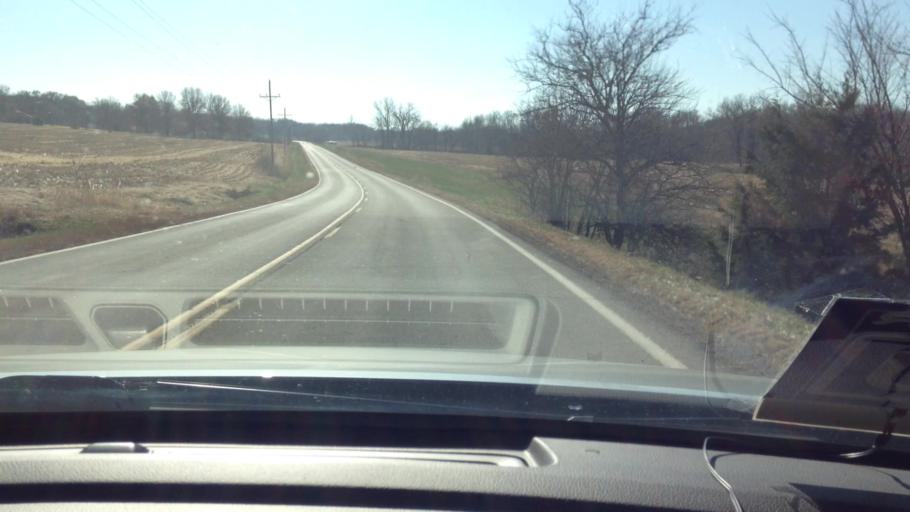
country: US
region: Missouri
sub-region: Platte County
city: Platte City
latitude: 39.4798
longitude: -94.8095
